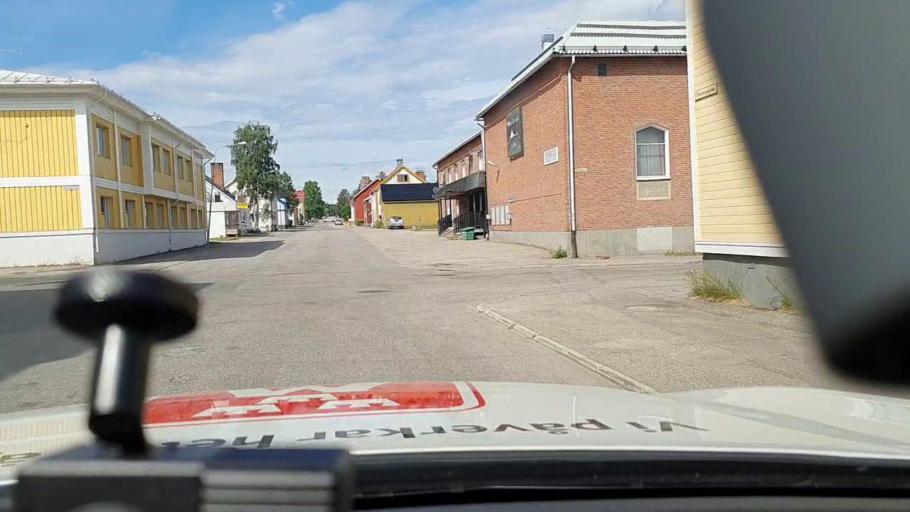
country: SE
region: Norrbotten
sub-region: Jokkmokks Kommun
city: Jokkmokk
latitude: 66.6072
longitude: 19.8300
